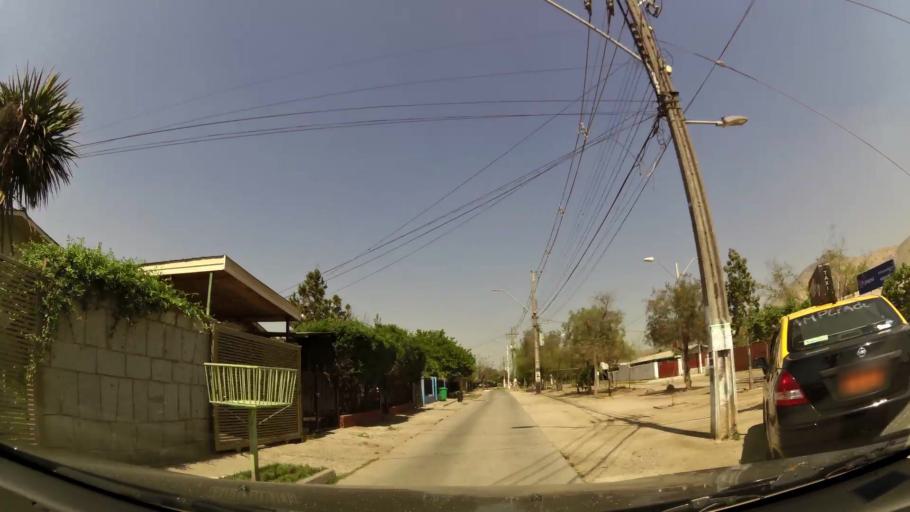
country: CL
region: Santiago Metropolitan
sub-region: Provincia de Maipo
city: San Bernardo
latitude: -33.5822
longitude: -70.7112
